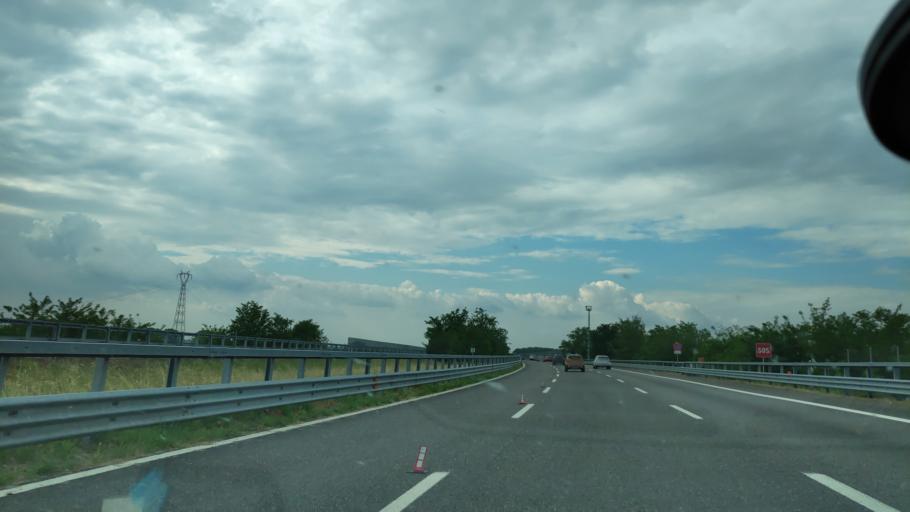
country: IT
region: Lombardy
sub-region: Provincia di Pavia
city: Corana
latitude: 45.0785
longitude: 8.9739
